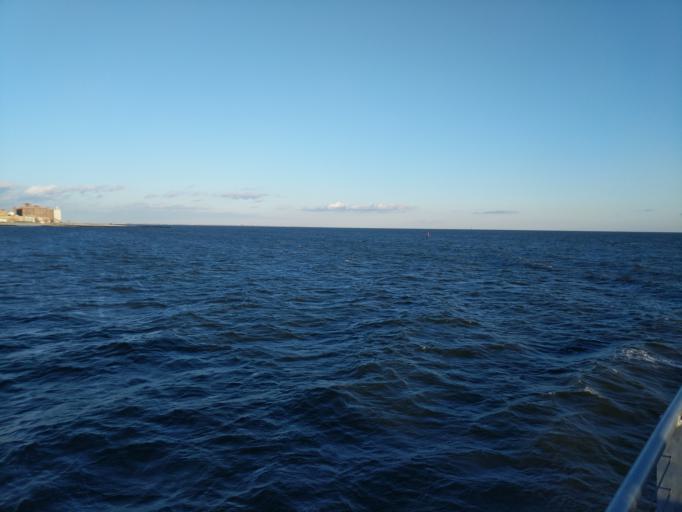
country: US
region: New York
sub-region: Kings County
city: Coney Island
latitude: 40.5711
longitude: -74.0140
